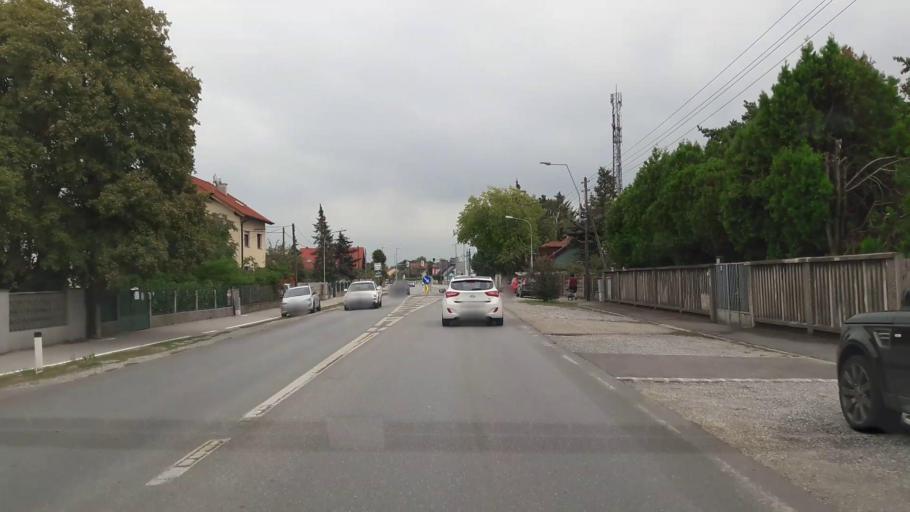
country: AT
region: Lower Austria
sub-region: Politischer Bezirk Ganserndorf
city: Strasshof an der Nordbahn
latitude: 48.3207
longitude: 16.6623
